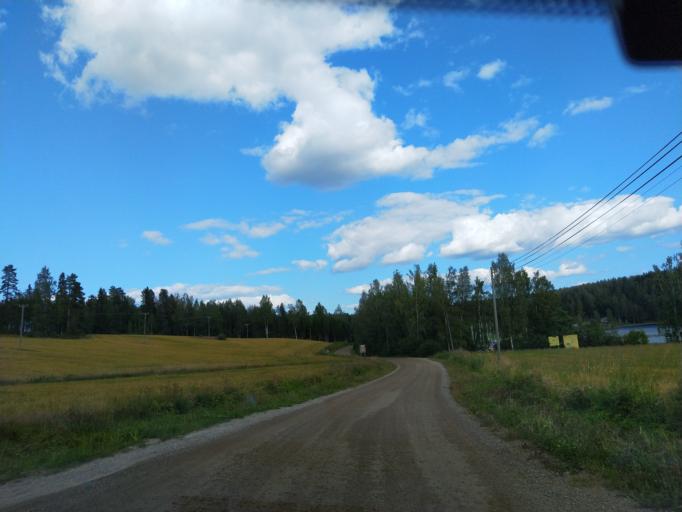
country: FI
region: Pirkanmaa
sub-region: Ylae-Pirkanmaa
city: Ruovesi
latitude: 61.9612
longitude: 24.0356
